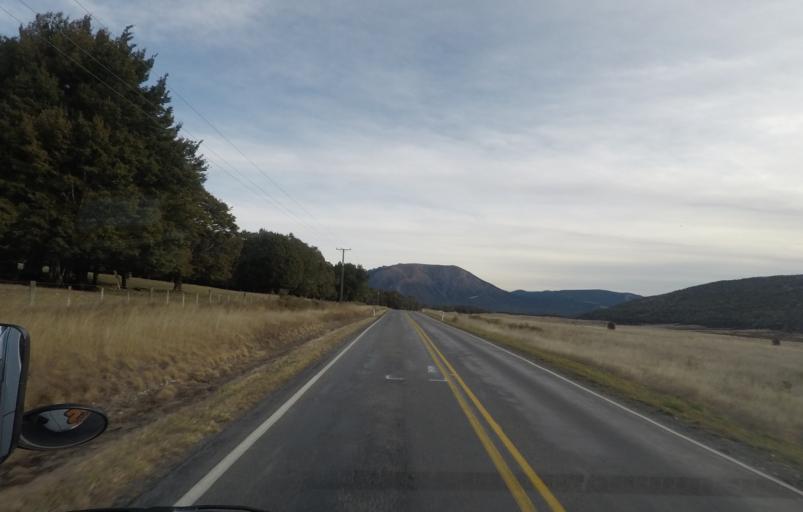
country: NZ
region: Tasman
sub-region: Tasman District
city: Wakefield
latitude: -41.7928
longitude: 172.8791
